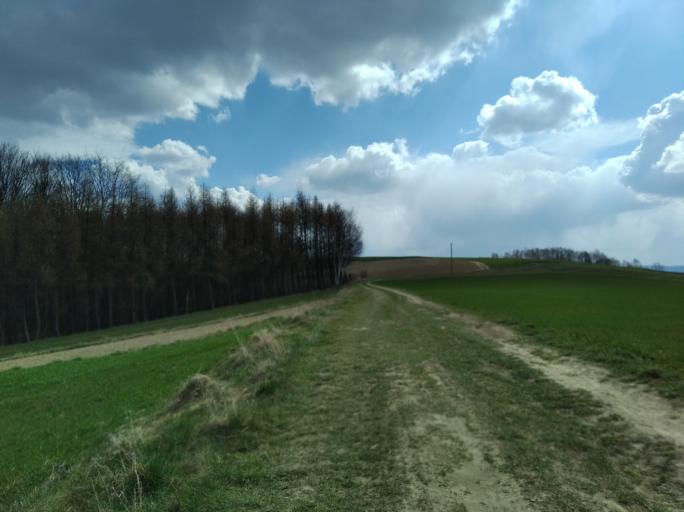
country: PL
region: Subcarpathian Voivodeship
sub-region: Powiat strzyzowski
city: Strzyzow
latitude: 49.9142
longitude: 21.7472
